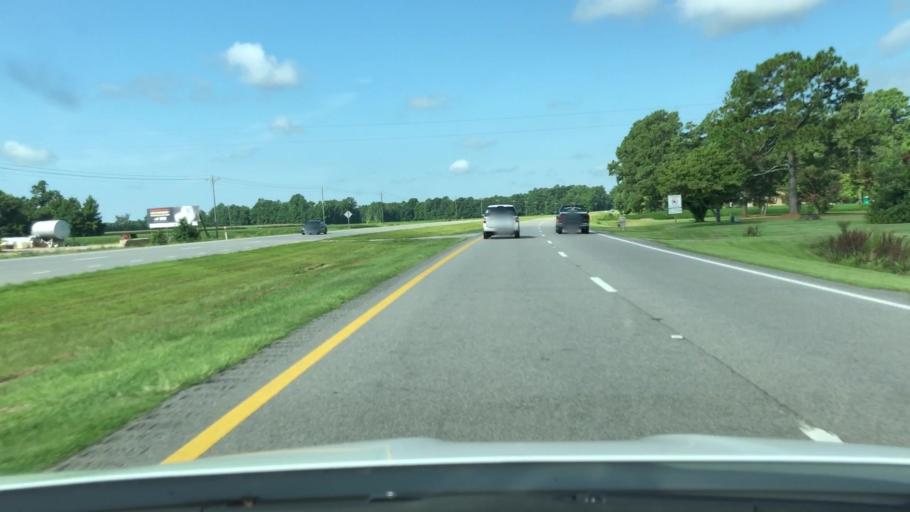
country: US
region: North Carolina
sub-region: Chowan County
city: Edenton
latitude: 36.0950
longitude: -76.5477
